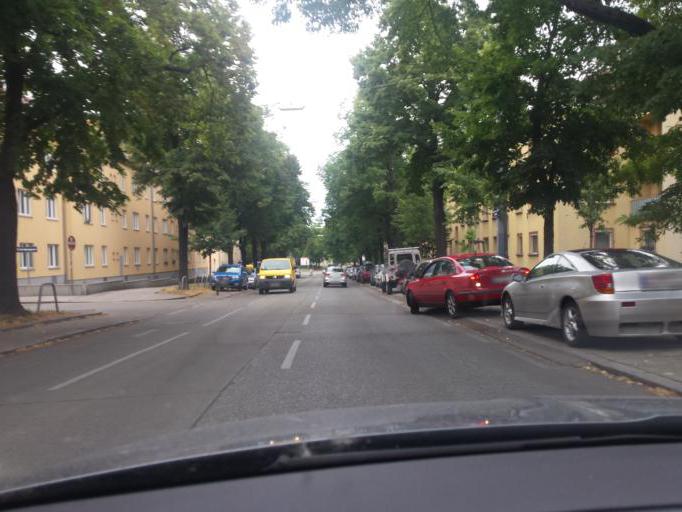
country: AT
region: Lower Austria
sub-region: Politischer Bezirk Wien-Umgebung
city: Leopoldsdorf
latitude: 48.1651
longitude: 16.4191
